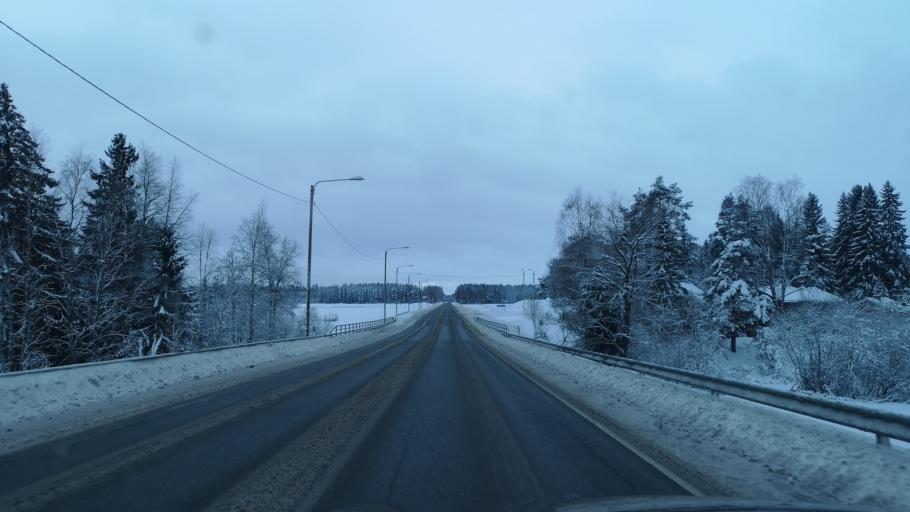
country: FI
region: Haeme
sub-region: Forssa
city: Ypaejae
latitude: 60.9190
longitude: 23.2002
